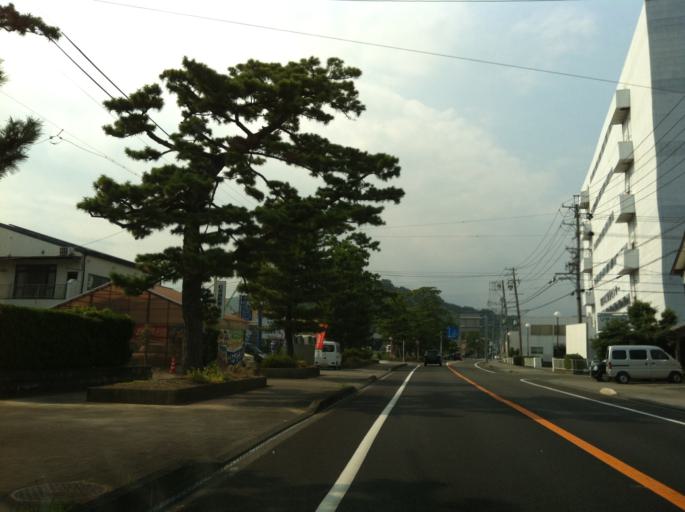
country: JP
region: Shizuoka
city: Fujieda
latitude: 34.9040
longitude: 138.2837
